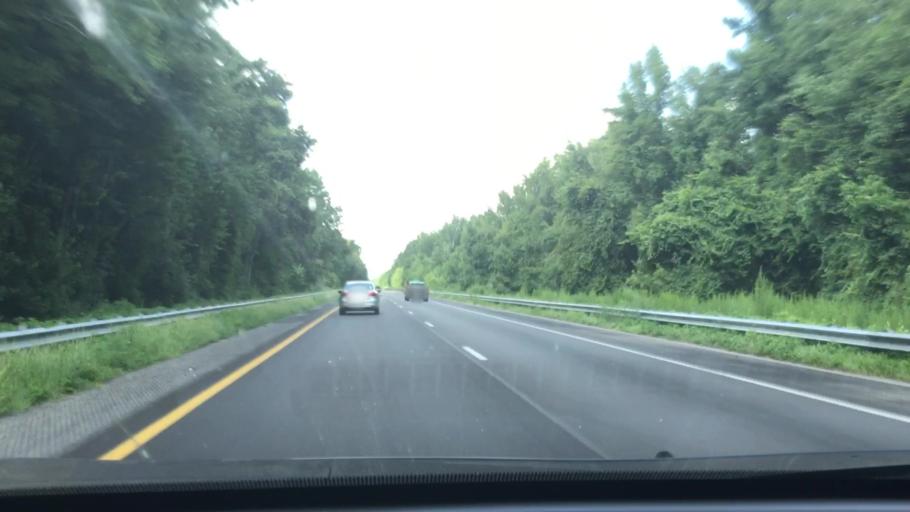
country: US
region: South Carolina
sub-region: Clarendon County
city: Manning
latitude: 33.8252
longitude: -80.1371
